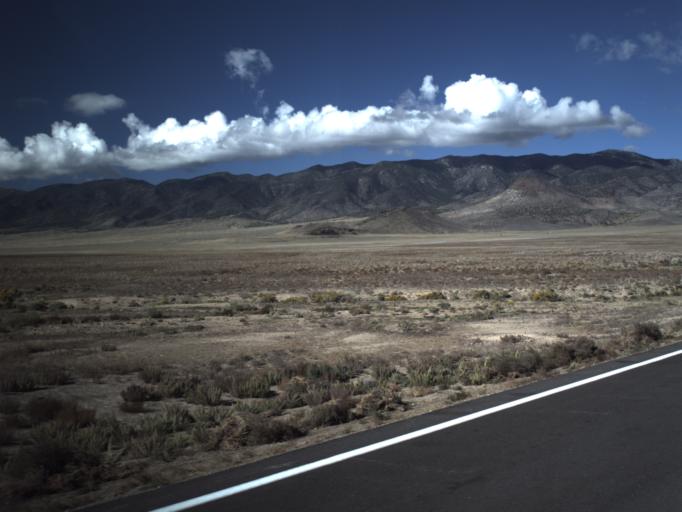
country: US
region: Utah
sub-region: Beaver County
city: Milford
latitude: 38.4763
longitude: -113.4247
